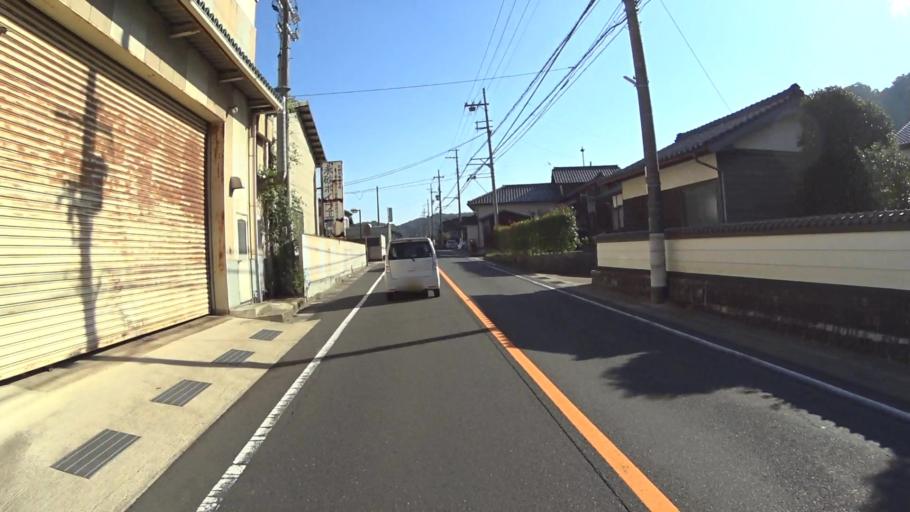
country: JP
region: Kyoto
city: Miyazu
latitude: 35.6600
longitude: 135.0315
